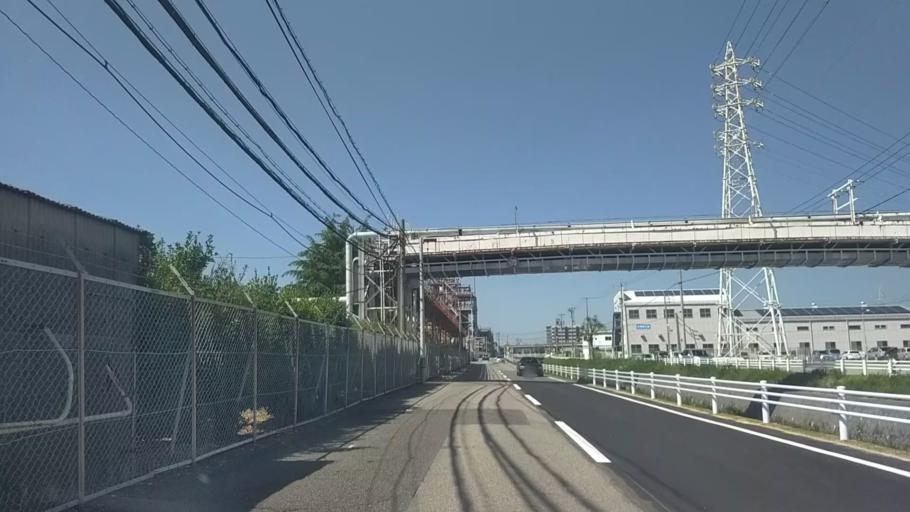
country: JP
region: Aichi
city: Okazaki
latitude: 34.9751
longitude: 137.1567
